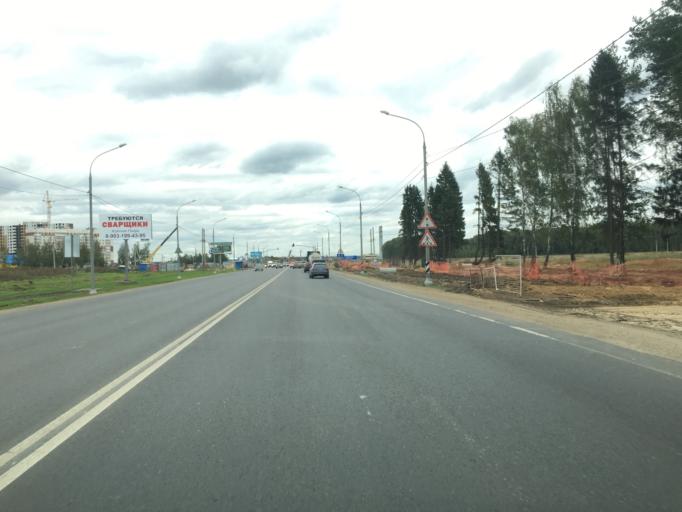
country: RU
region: Moskovskaya
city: Vatutinki
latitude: 55.5101
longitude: 37.3517
